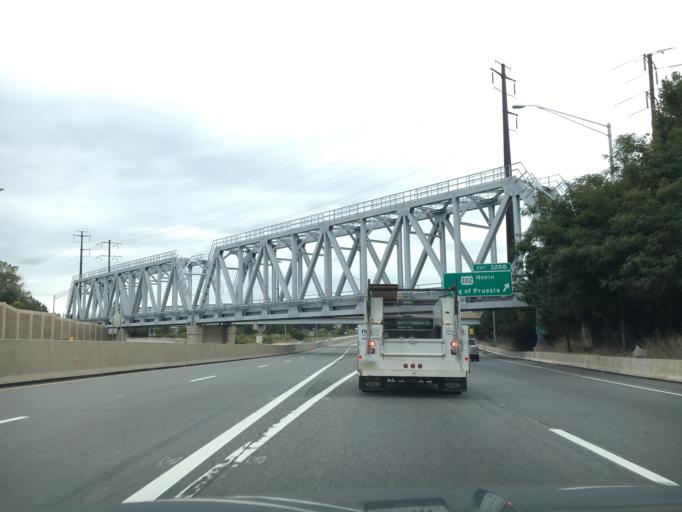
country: US
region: Pennsylvania
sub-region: Montgomery County
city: King of Prussia
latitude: 40.0816
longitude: -75.3879
